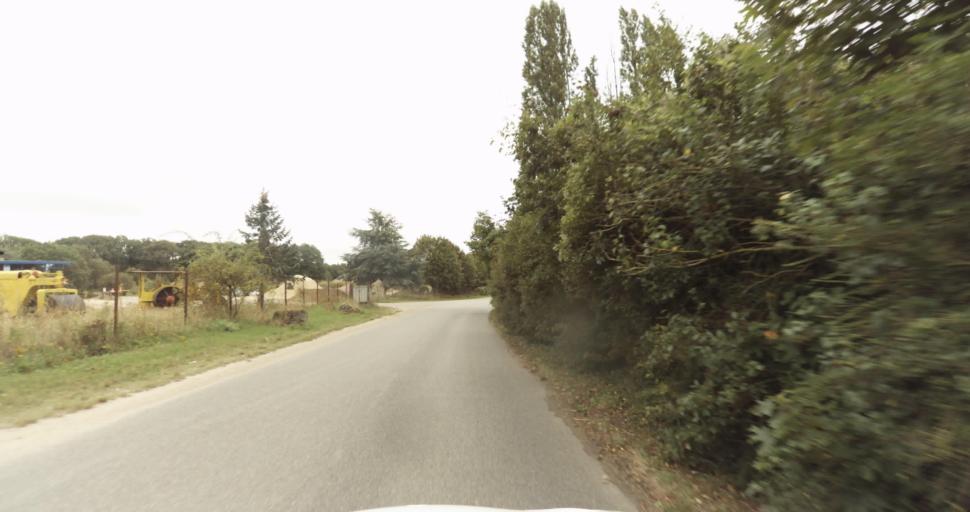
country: FR
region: Haute-Normandie
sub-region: Departement de l'Eure
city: Gravigny
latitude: 49.0402
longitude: 1.1740
